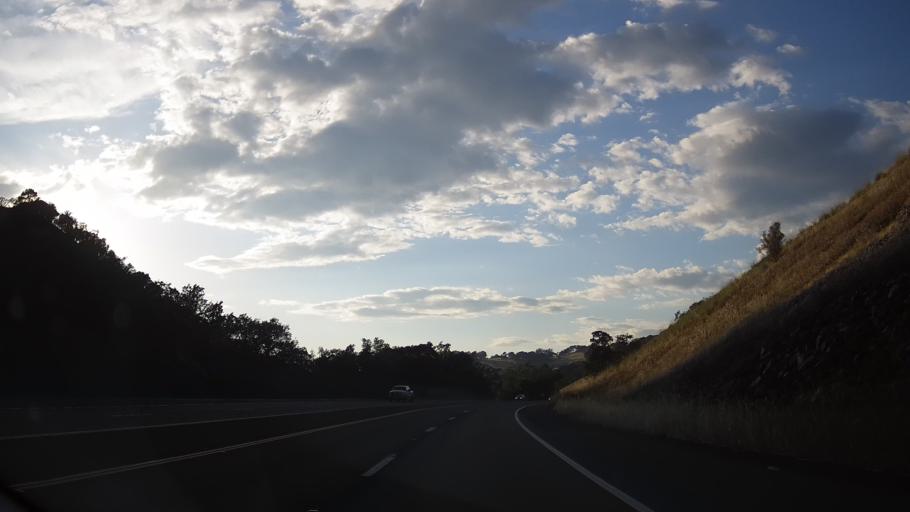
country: US
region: California
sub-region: Sonoma County
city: Cloverdale
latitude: 38.9322
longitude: -123.0610
